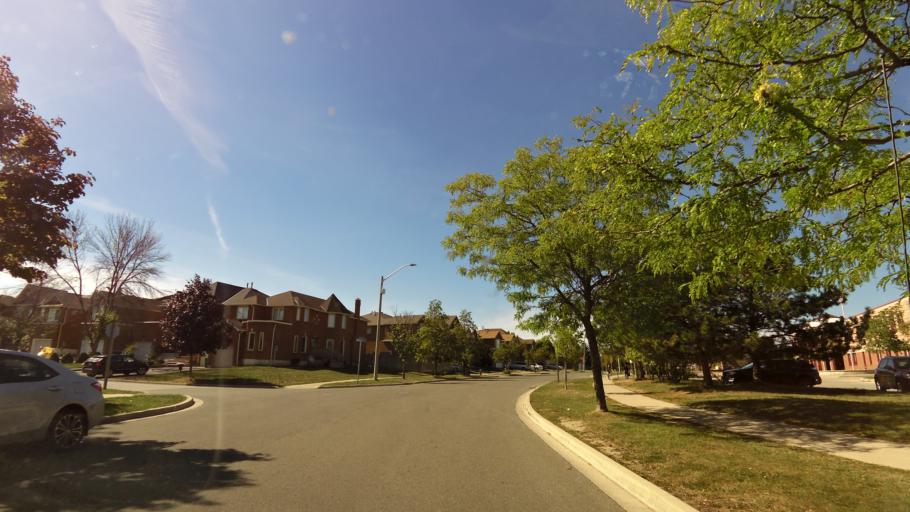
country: CA
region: Ontario
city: Mississauga
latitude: 43.6046
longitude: -79.6656
